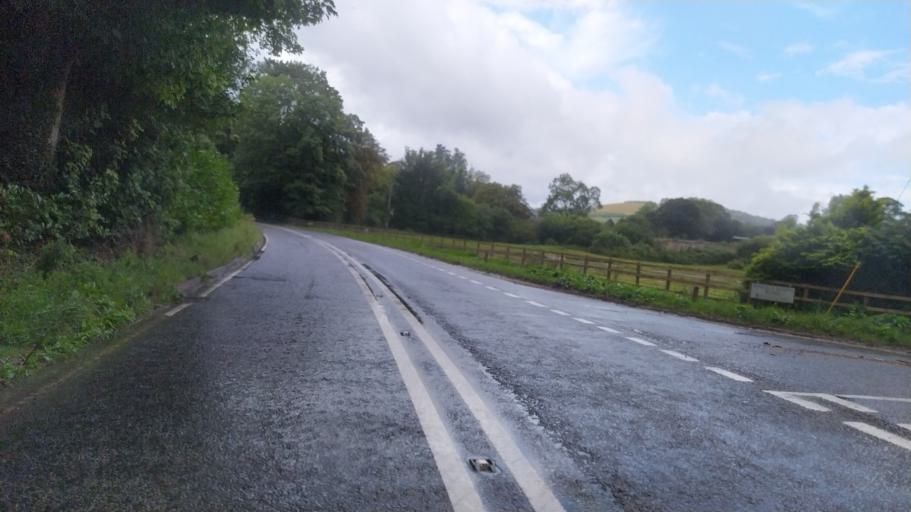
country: GB
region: England
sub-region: Hampshire
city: Swanmore
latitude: 51.0038
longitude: -1.1156
